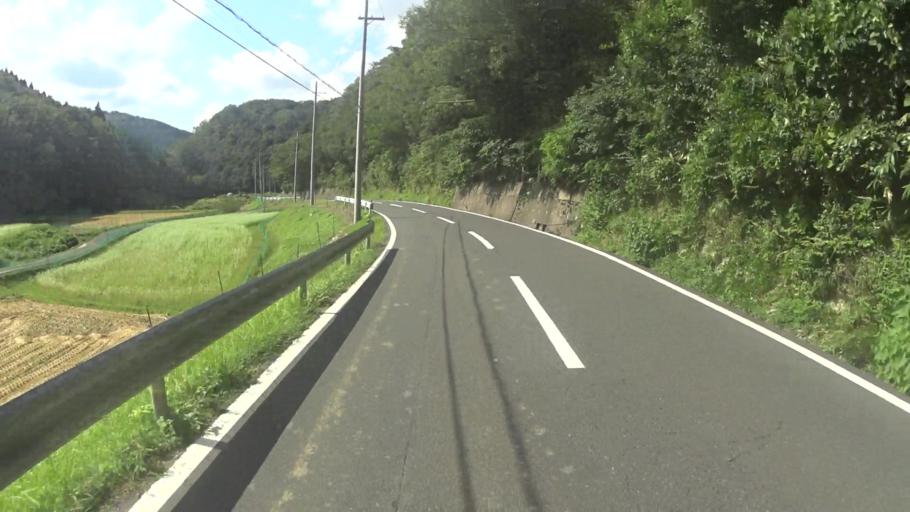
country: JP
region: Kyoto
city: Miyazu
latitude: 35.7088
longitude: 135.2715
